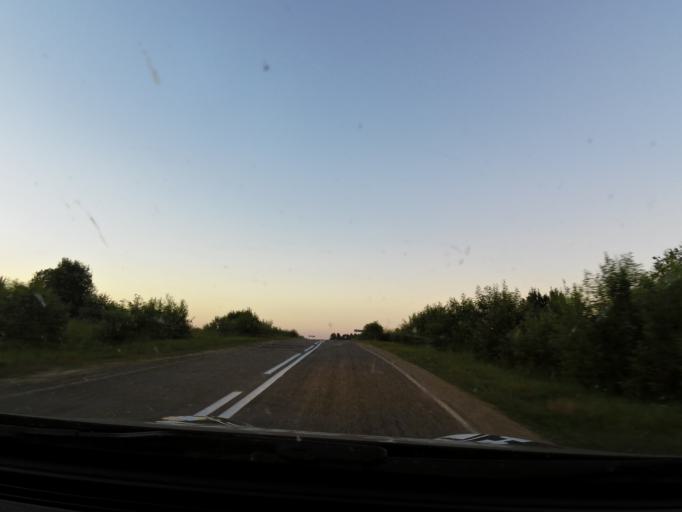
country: RU
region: Jaroslavl
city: Lyubim
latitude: 58.3411
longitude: 41.1188
